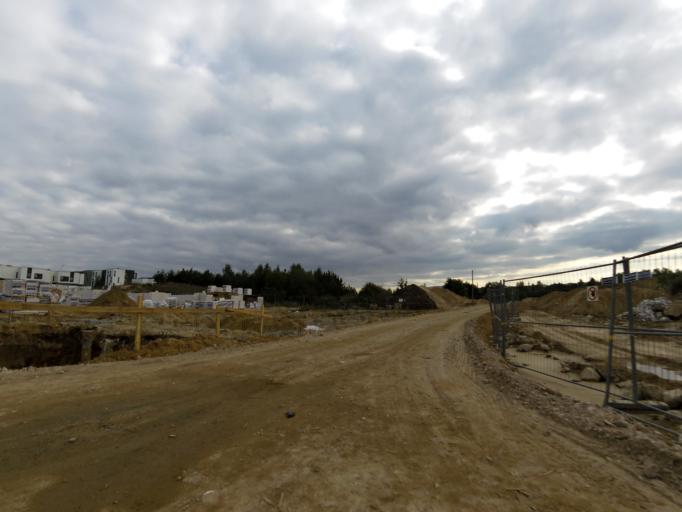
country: LT
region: Vilnius County
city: Pilaite
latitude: 54.7072
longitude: 25.1683
